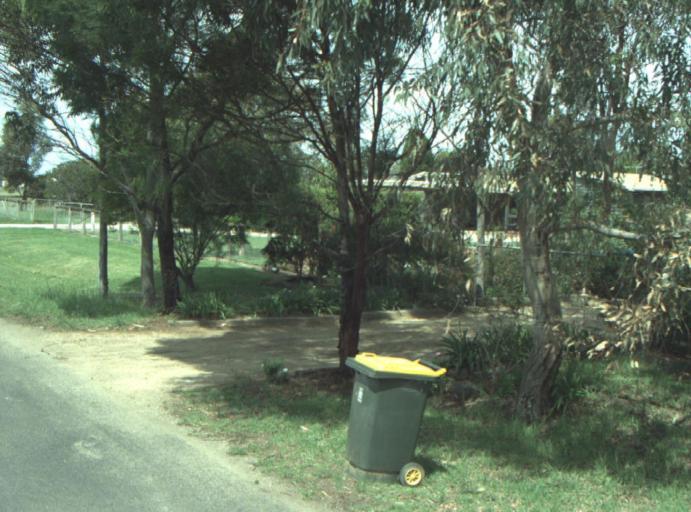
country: AU
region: Victoria
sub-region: Wyndham
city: Little River
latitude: -37.9651
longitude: 144.5074
